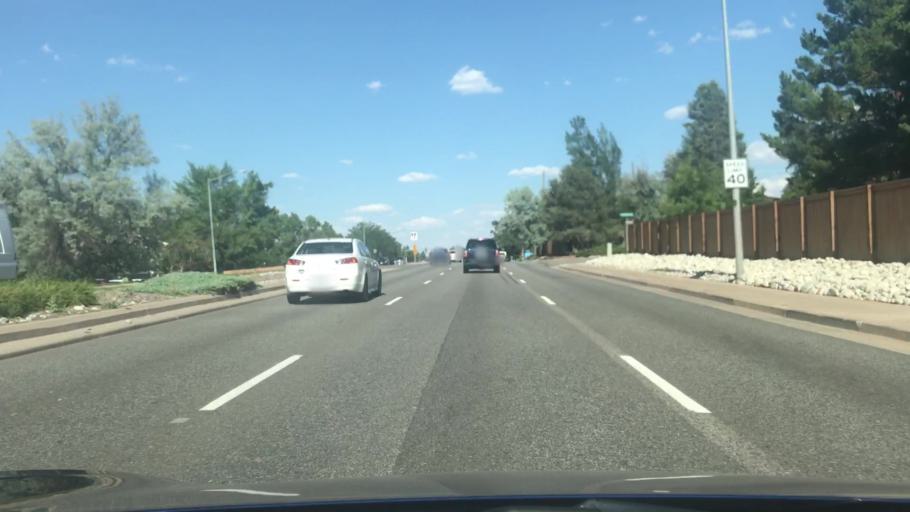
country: US
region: Colorado
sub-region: Arapahoe County
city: Dove Valley
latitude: 39.6530
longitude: -104.8161
